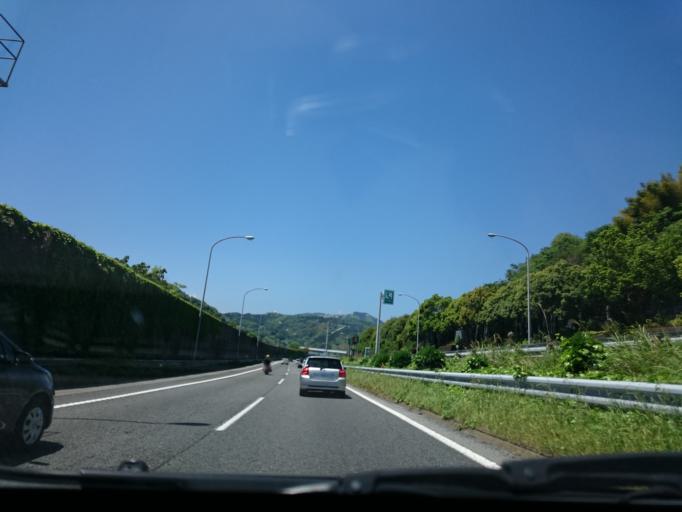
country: JP
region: Kanagawa
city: Odawara
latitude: 35.3591
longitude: 139.1078
